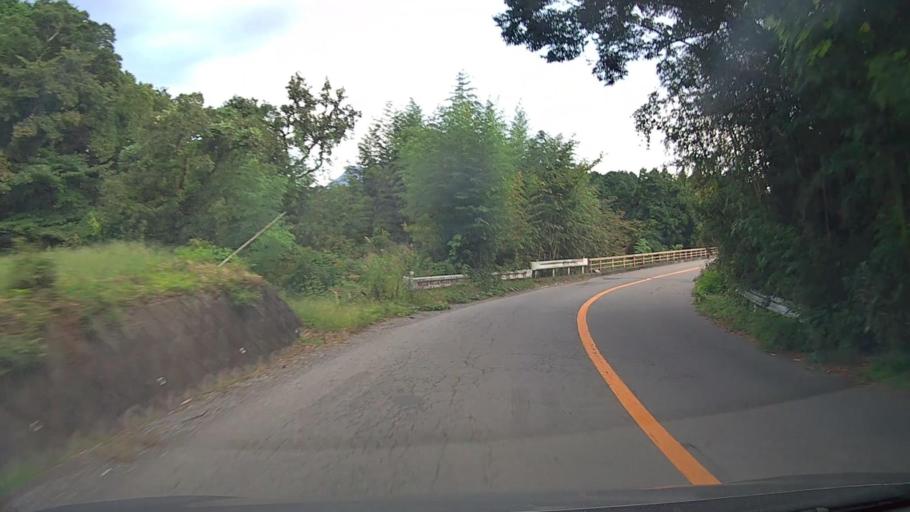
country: JP
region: Shizuoka
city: Gotemba
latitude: 35.3418
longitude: 138.9586
